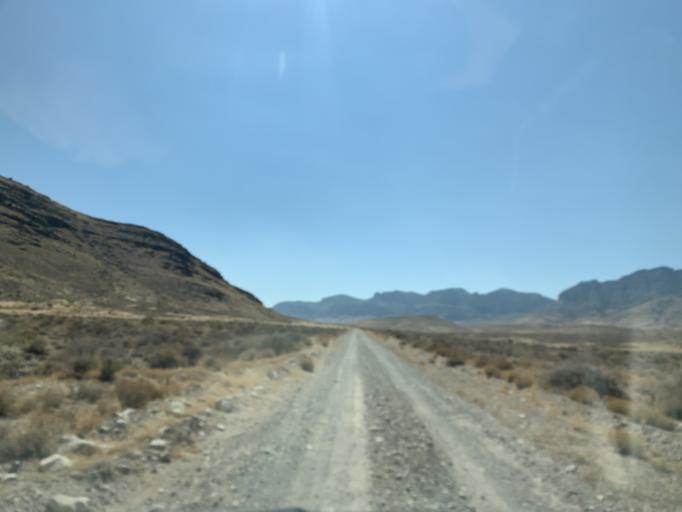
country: US
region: Utah
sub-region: Beaver County
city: Milford
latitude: 38.9853
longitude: -113.4405
